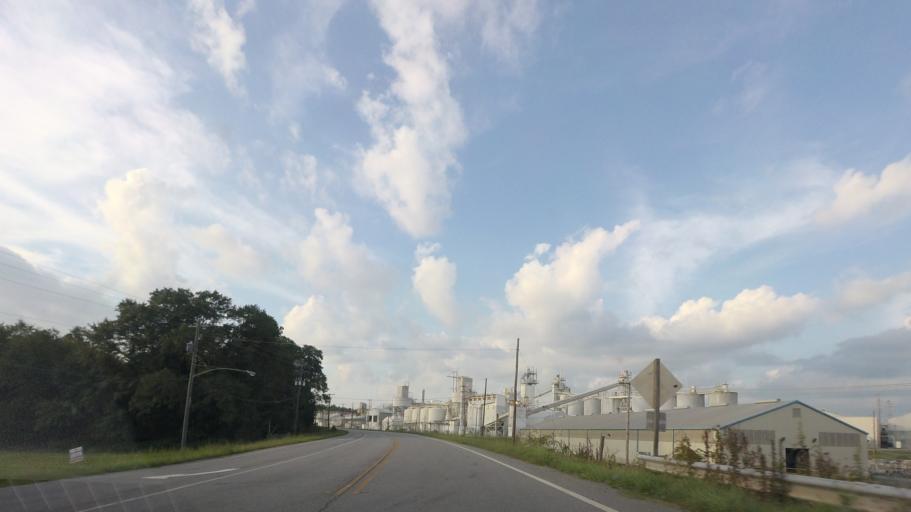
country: US
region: Georgia
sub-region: Wilkinson County
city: Gordon
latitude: 32.8782
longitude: -83.3398
